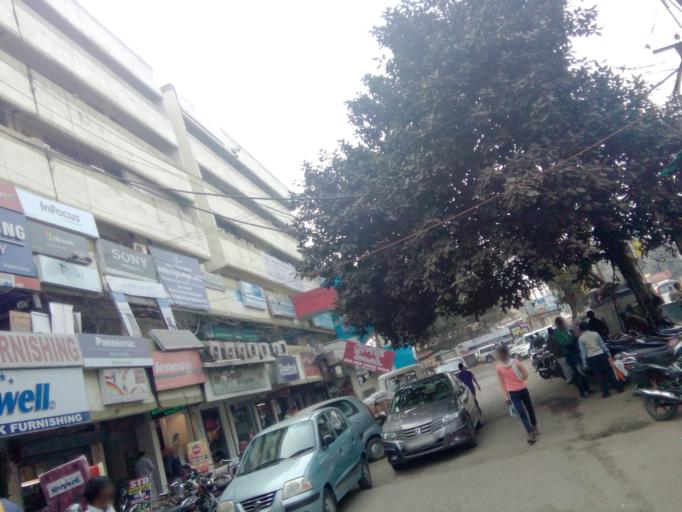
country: IN
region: Bihar
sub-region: Patna
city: Patna
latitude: 25.6102
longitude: 85.1346
